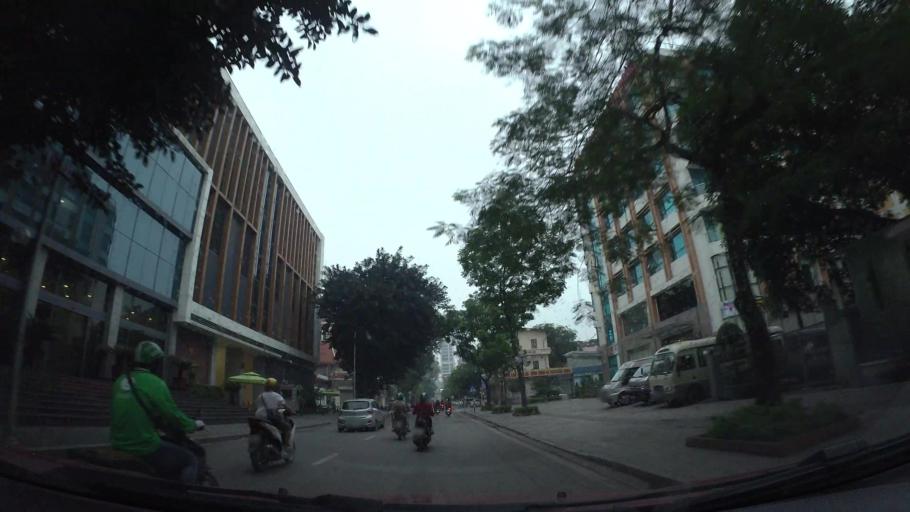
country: VN
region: Ha Noi
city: Hanoi
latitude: 21.0205
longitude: 105.8427
